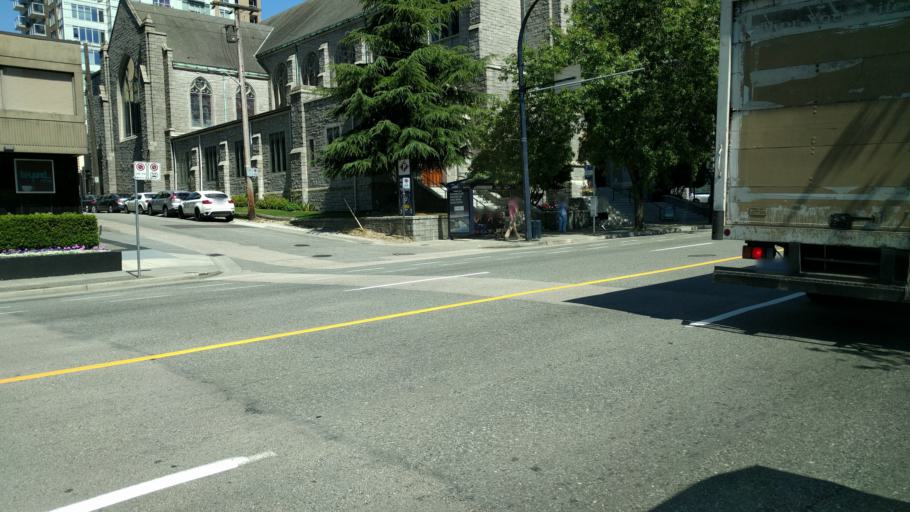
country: CA
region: British Columbia
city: West End
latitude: 49.2808
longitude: -123.1266
